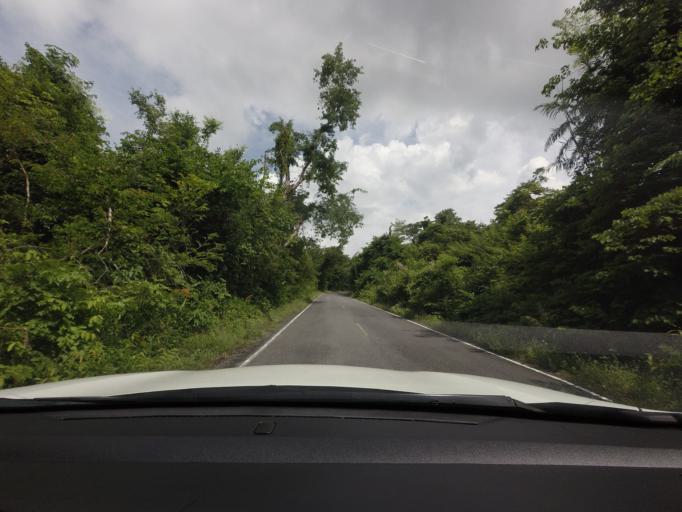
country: TH
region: Nakhon Nayok
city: Pak Phli
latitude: 14.2450
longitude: 101.3872
